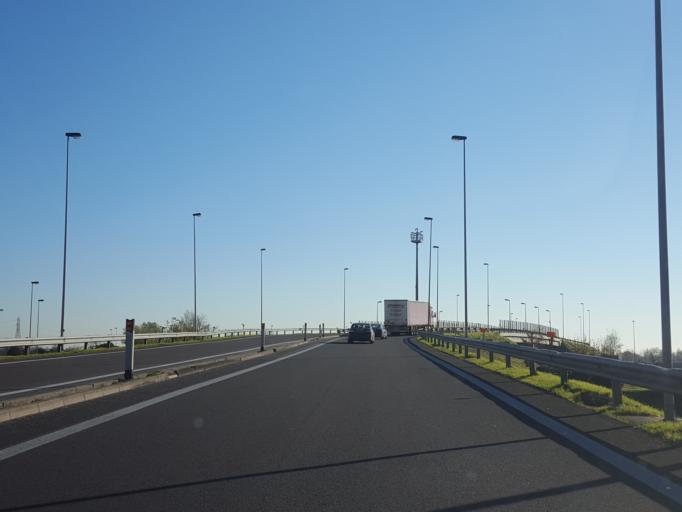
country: IT
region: Veneto
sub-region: Provincia di Verona
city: San Martino Buon Albergo
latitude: 45.4123
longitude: 11.0899
